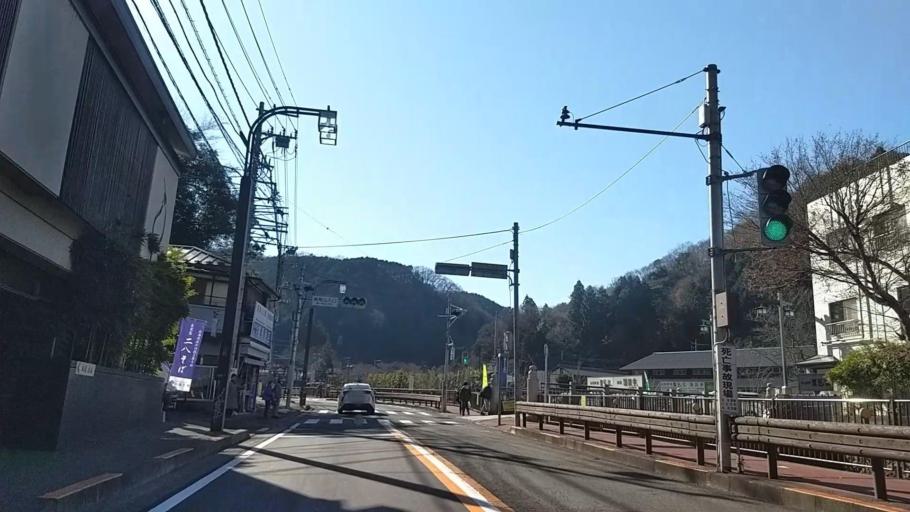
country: JP
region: Tokyo
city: Hachioji
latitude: 35.6312
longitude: 139.2697
